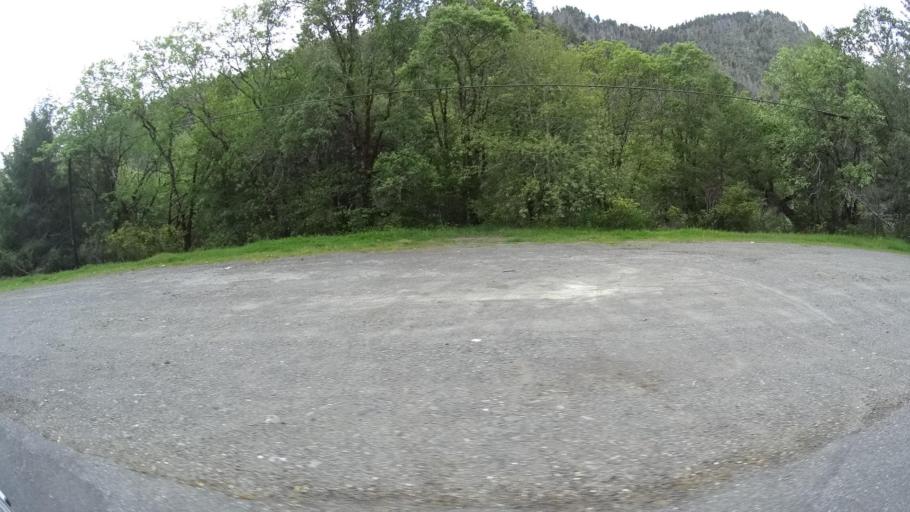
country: US
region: California
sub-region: Humboldt County
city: Redway
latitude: 40.2248
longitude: -123.6060
